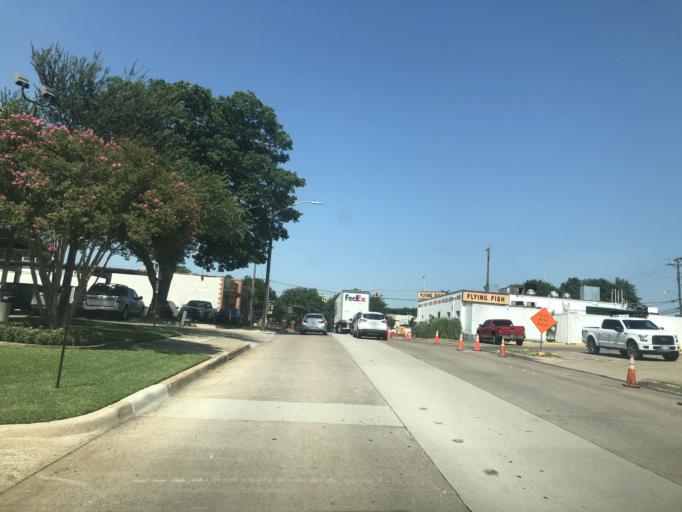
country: US
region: Texas
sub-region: Tarrant County
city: Fort Worth
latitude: 32.7309
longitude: -97.3691
